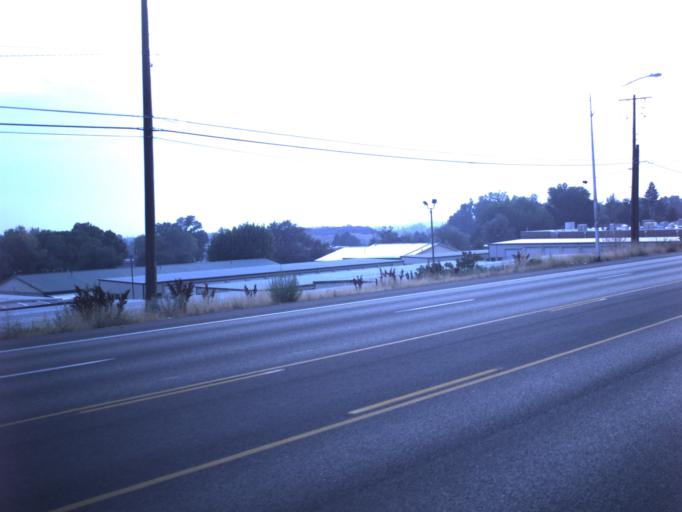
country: US
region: Utah
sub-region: Utah County
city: Springville
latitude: 40.2027
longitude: -111.6230
